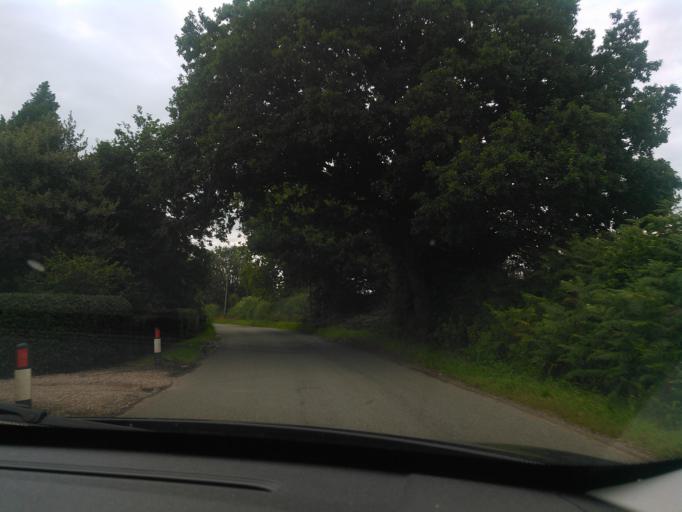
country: GB
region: England
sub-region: Shropshire
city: Prees
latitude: 52.8657
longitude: -2.6649
